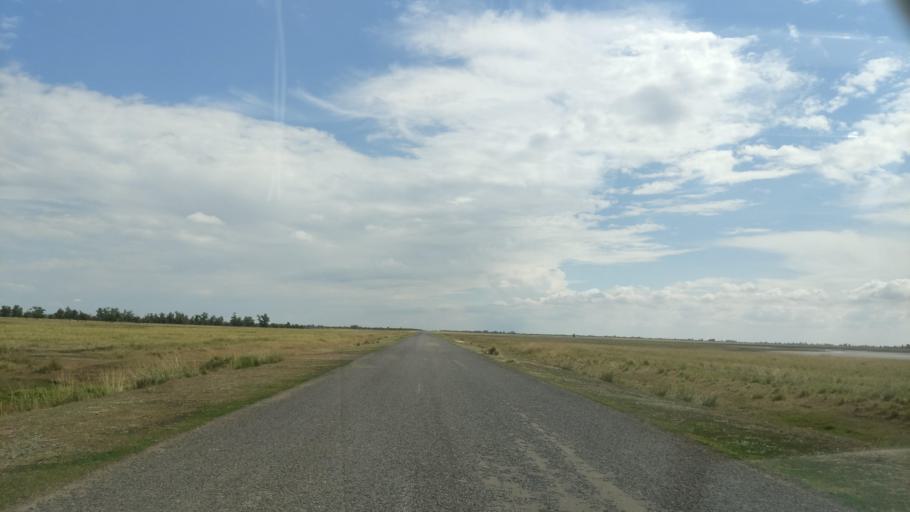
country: KZ
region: Pavlodar
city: Pavlodar
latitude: 52.6354
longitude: 76.9280
